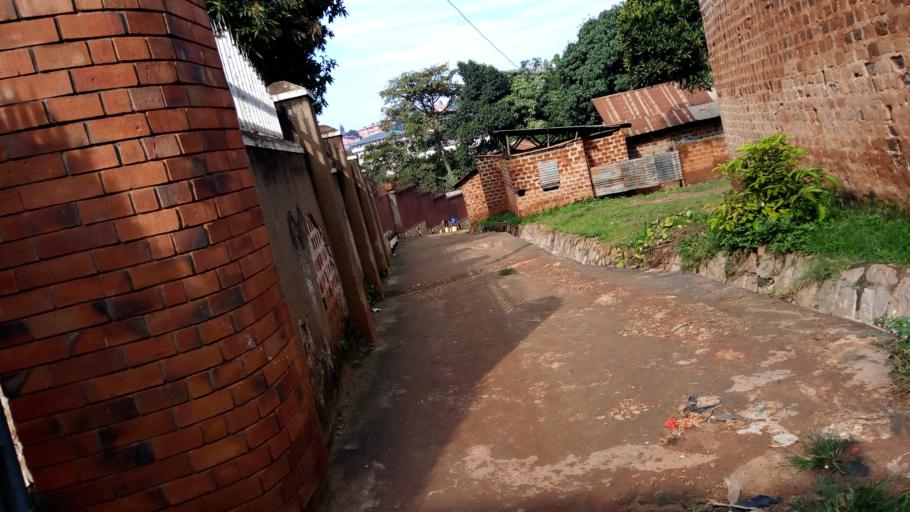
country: UG
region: Central Region
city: Kampala Central Division
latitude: 0.3704
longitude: 32.5553
